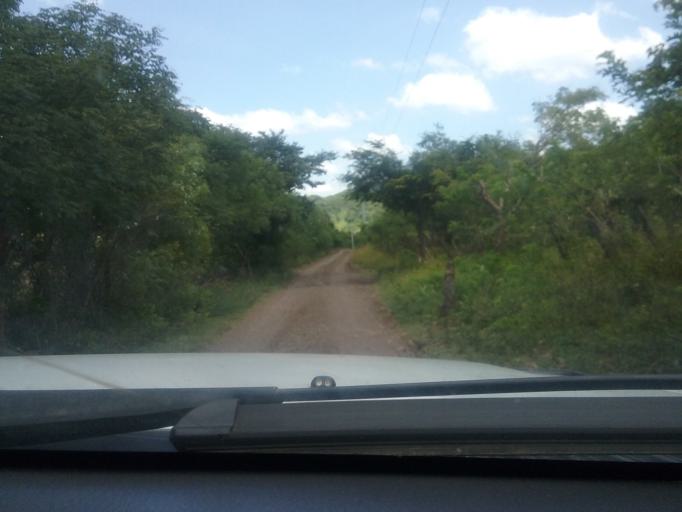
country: NI
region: Matagalpa
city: Terrabona
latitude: 12.6529
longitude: -86.0021
